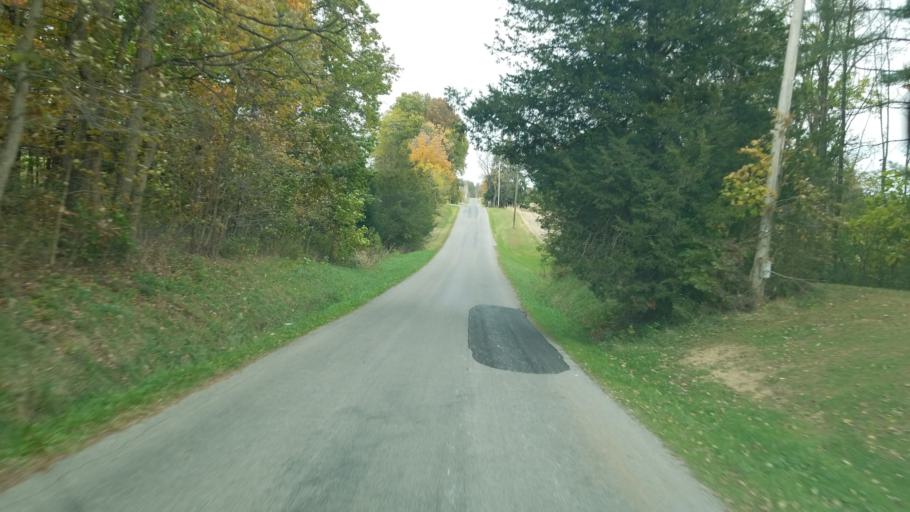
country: US
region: Ohio
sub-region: Ashland County
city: Ashland
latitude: 40.8826
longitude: -82.2401
